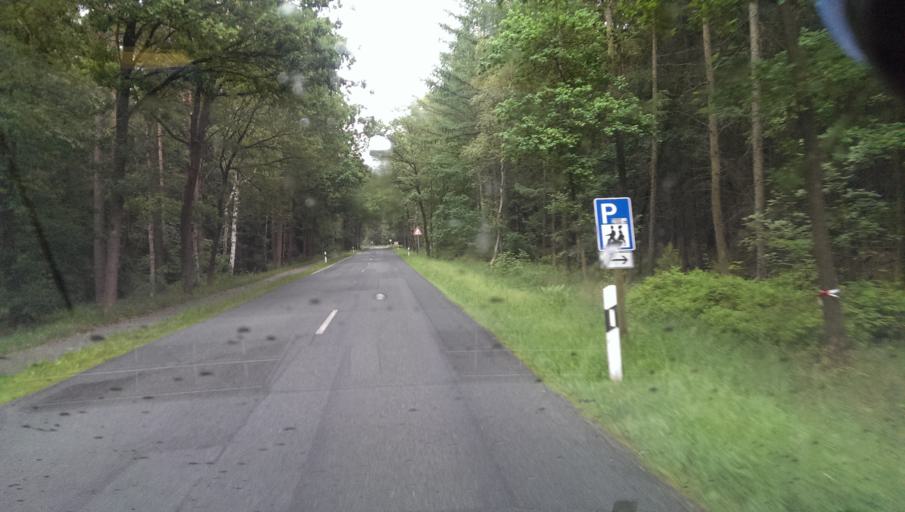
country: DE
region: Lower Saxony
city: Hermannsburg
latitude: 52.7921
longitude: 10.1215
